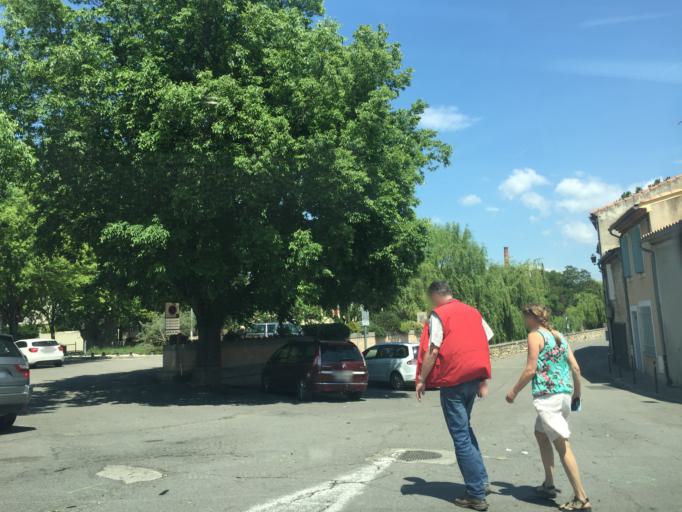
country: FR
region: Provence-Alpes-Cote d'Azur
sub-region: Departement du Vaucluse
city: Pernes-les-Fontaines
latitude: 43.9981
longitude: 5.0554
